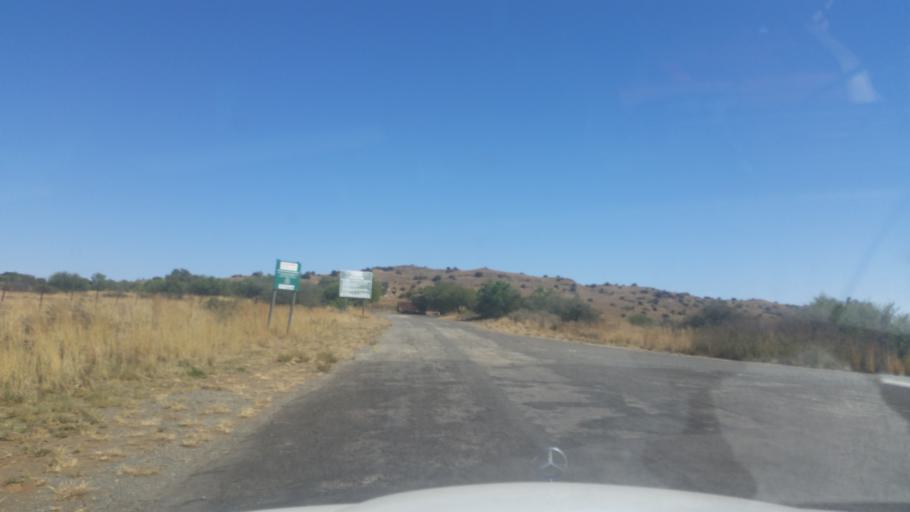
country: ZA
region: Eastern Cape
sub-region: Joe Gqabi District Municipality
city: Burgersdorp
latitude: -30.7440
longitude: 25.7565
